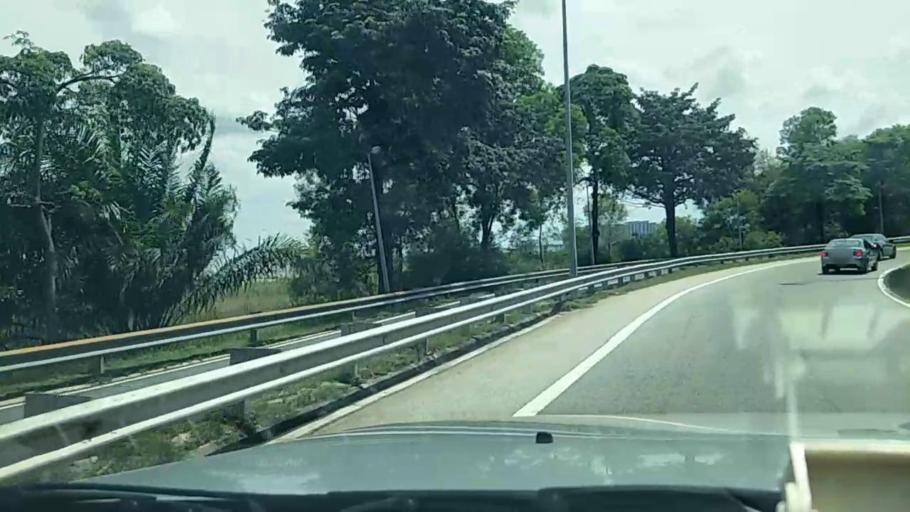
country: MY
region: Selangor
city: Subang Jaya
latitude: 3.0550
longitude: 101.6161
